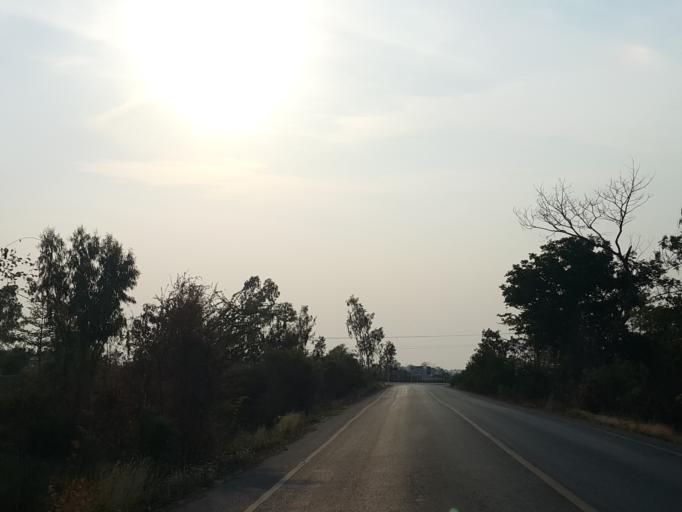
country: TH
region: Sukhothai
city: Si Samrong
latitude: 17.2115
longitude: 99.9502
